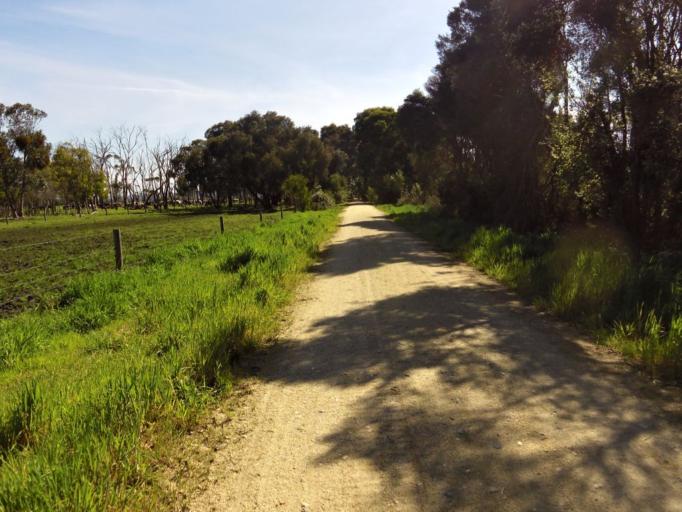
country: AU
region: Victoria
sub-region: Latrobe
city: Morwell
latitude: -38.6639
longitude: 146.2456
